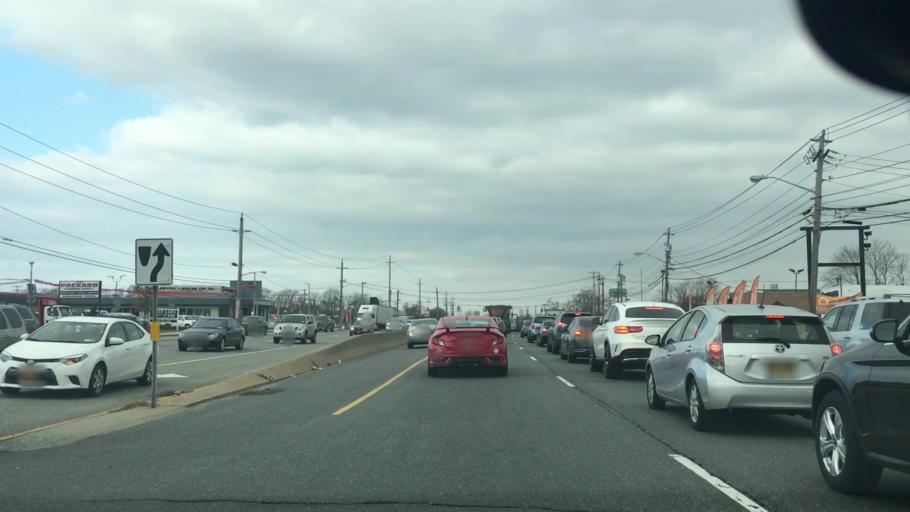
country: US
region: New York
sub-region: Suffolk County
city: East Farmingdale
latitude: 40.7450
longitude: -73.4226
